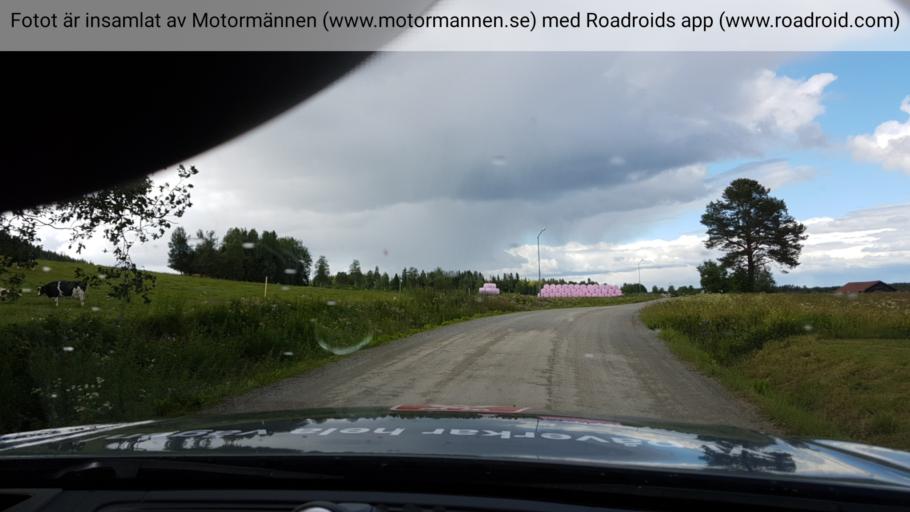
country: SE
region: Jaemtland
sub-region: Bergs Kommun
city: Hoverberg
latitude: 62.9392
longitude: 14.2723
